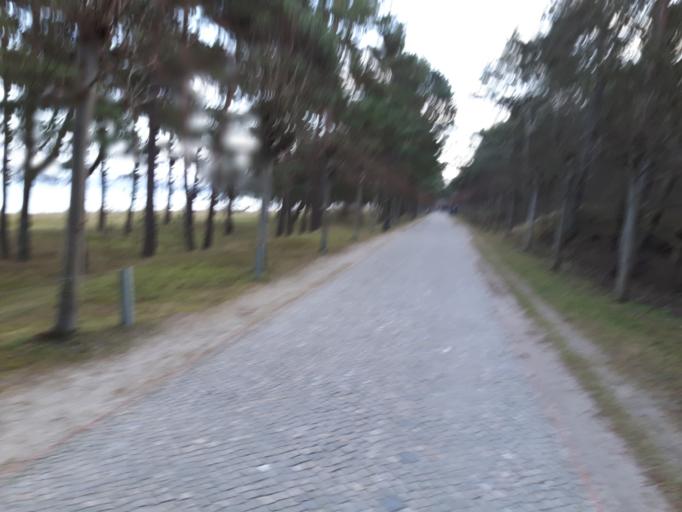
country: DE
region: Mecklenburg-Vorpommern
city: Ostseebad Binz
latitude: 54.4171
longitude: 13.5941
